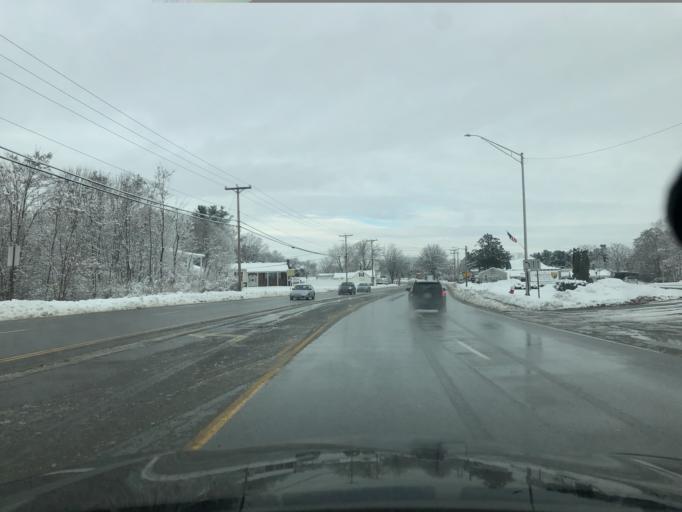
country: US
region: New Hampshire
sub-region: Strafford County
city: Somersworth
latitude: 43.2372
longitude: -70.8804
